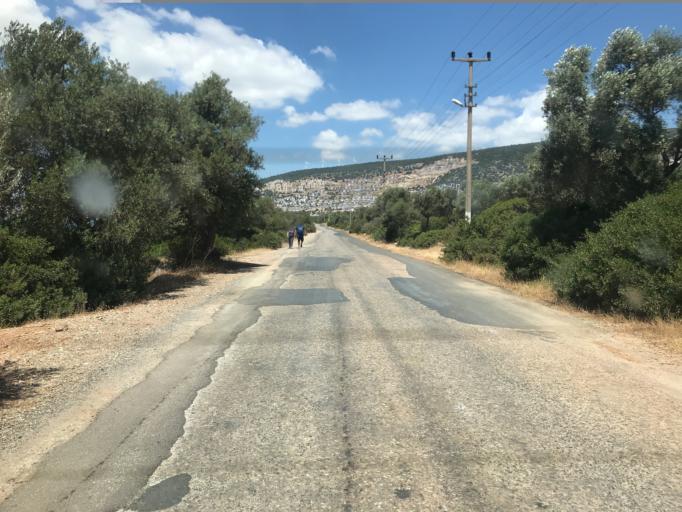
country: TR
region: Aydin
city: Sarikemer
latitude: 37.4084
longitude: 27.4247
